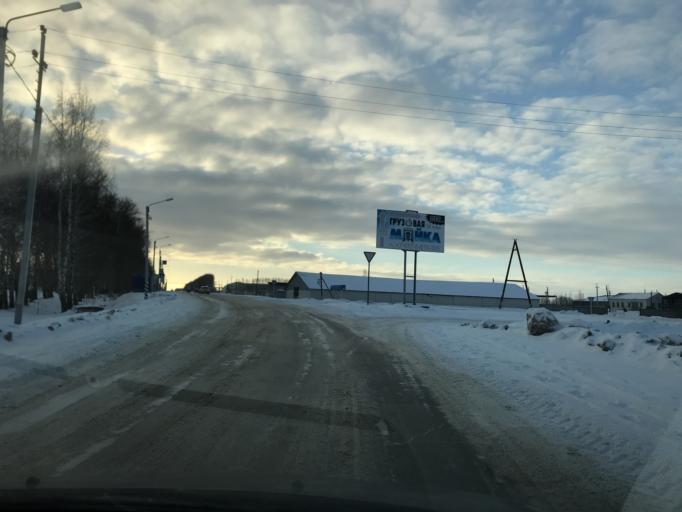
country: RU
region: Ulyanovsk
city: Undory
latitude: 54.6095
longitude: 48.3822
